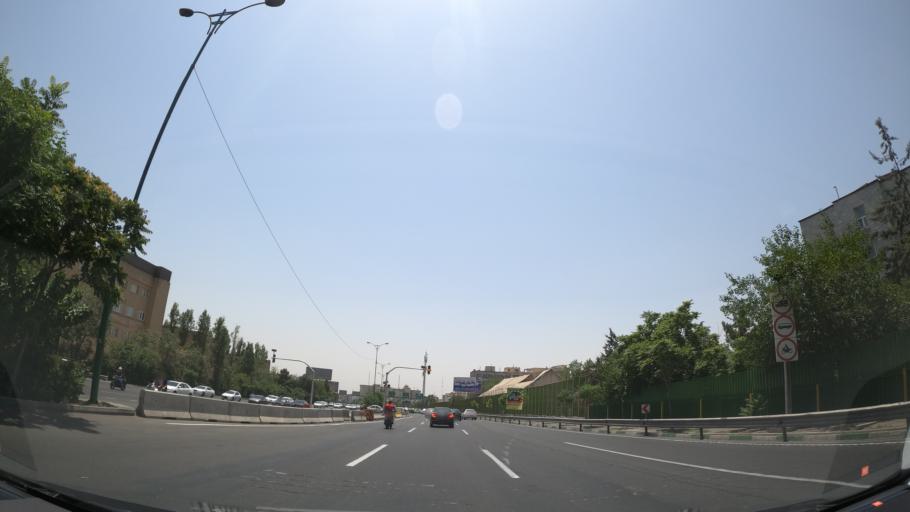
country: IR
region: Tehran
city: Tehran
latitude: 35.7209
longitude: 51.3788
